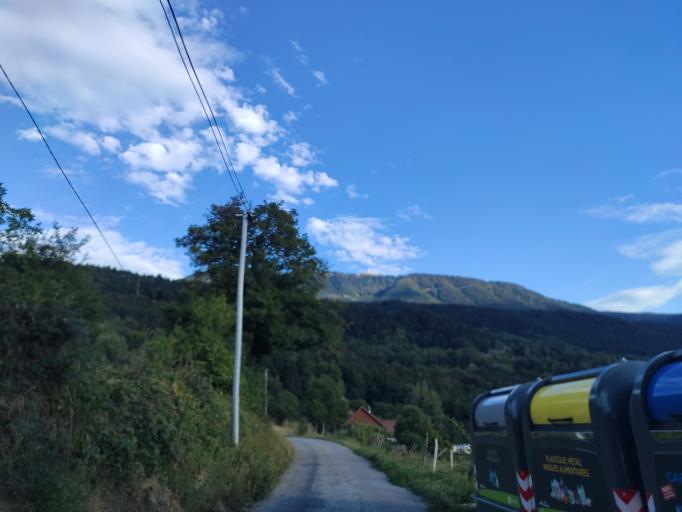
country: FR
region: Rhone-Alpes
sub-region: Departement de l'Isere
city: Revel
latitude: 45.1576
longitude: 5.8570
